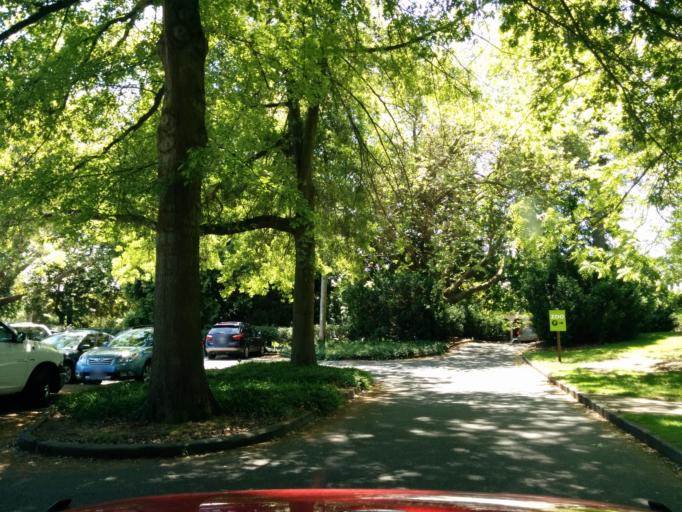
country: US
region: Washington
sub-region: King County
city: Seattle
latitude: 47.6656
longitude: -122.3517
